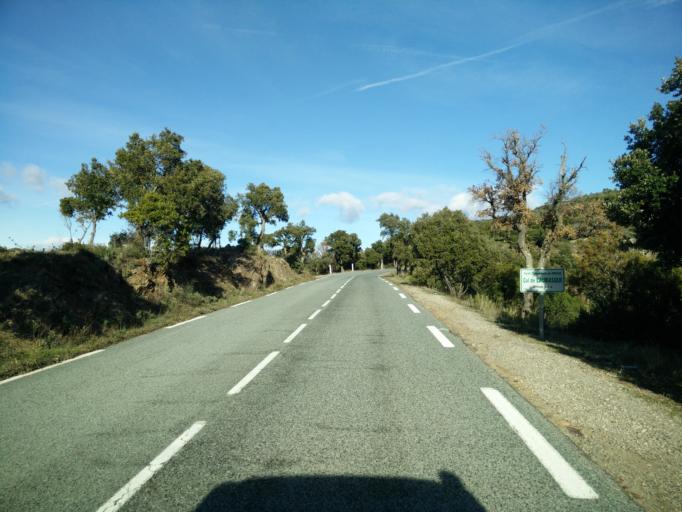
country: FR
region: Provence-Alpes-Cote d'Azur
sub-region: Departement du Var
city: Saint-Raphael
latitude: 43.4936
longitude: 6.7786
